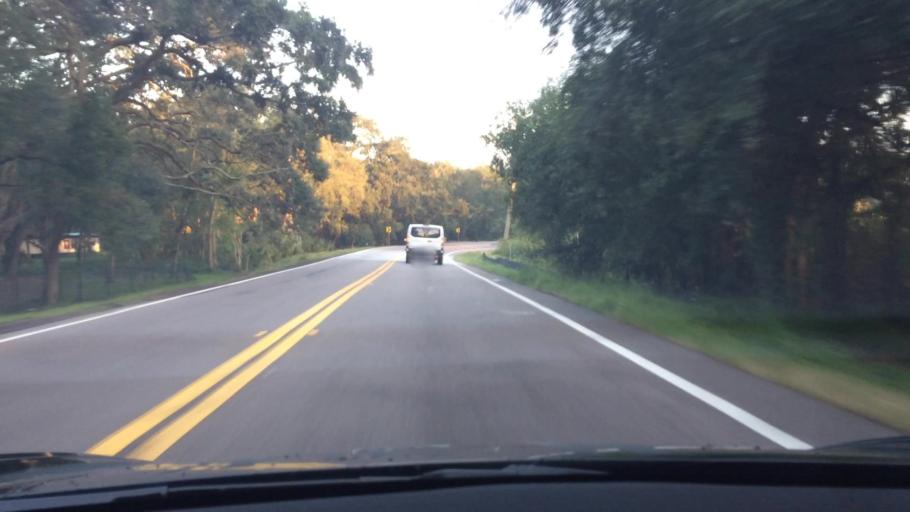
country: US
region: Florida
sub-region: Hillsborough County
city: Citrus Park
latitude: 28.1089
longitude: -82.5811
